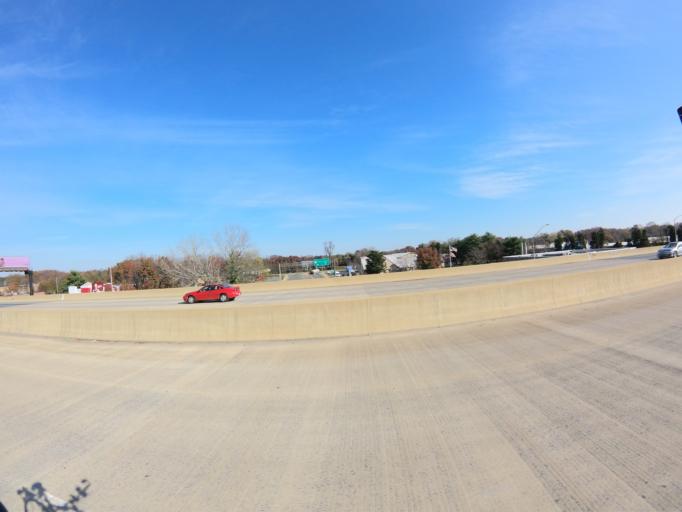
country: US
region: Maryland
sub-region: Prince George's County
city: Clinton
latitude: 38.7828
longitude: -76.8946
